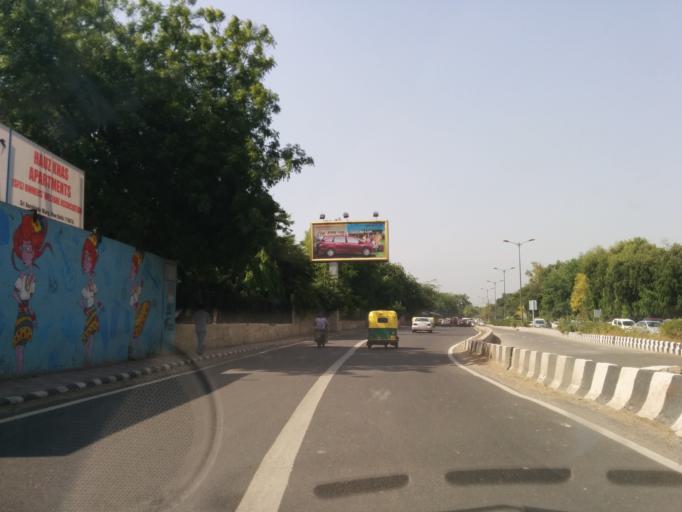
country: IN
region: NCT
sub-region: New Delhi
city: New Delhi
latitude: 28.5559
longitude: 77.2063
